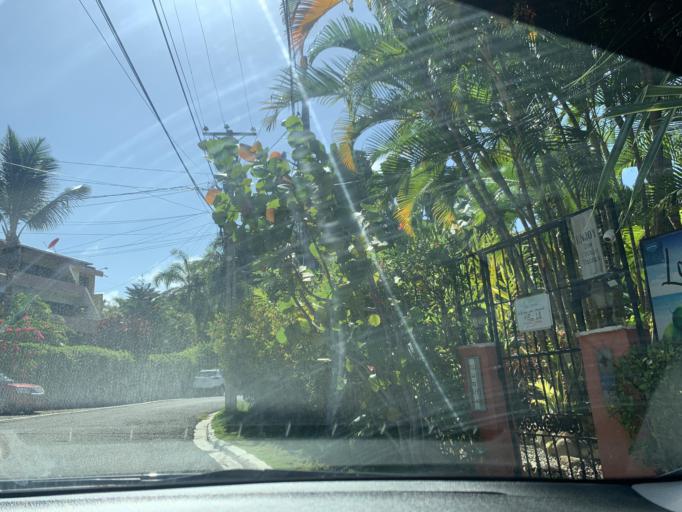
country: DO
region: Puerto Plata
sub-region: Puerto Plata
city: Puerto Plata
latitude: 19.8069
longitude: -70.7270
